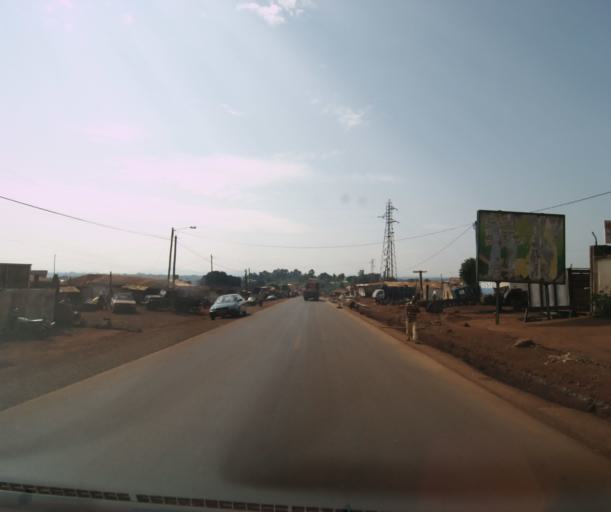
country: CM
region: West
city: Mbouda
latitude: 5.6227
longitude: 10.2653
